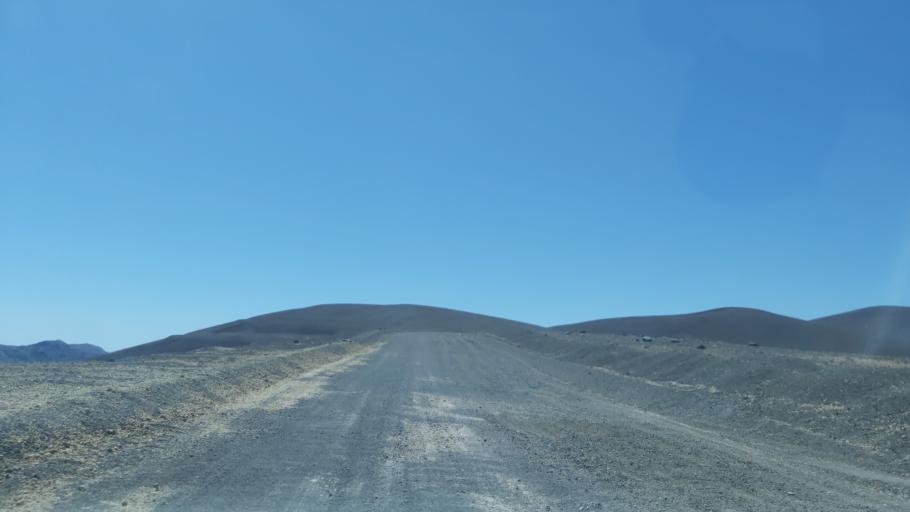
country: CL
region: Araucania
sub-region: Provincia de Cautin
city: Vilcun
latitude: -38.3751
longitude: -71.5400
